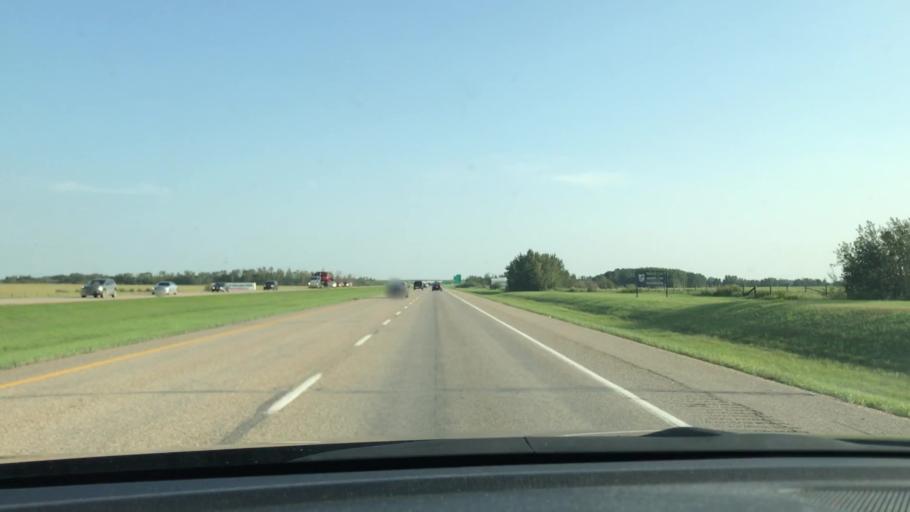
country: CA
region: Alberta
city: Millet
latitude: 53.1057
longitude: -113.5984
